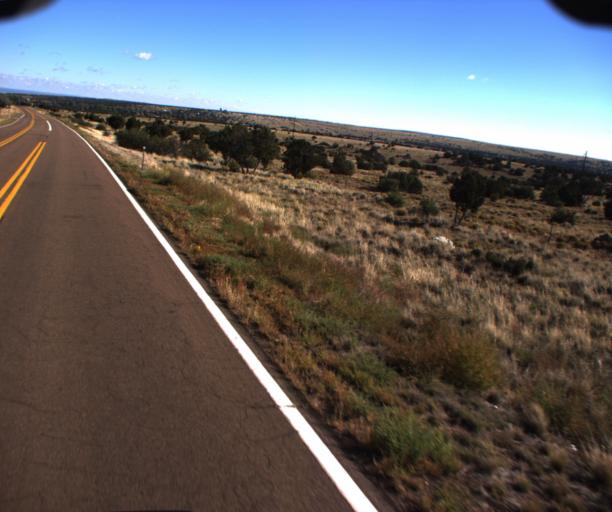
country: US
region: Arizona
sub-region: Apache County
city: Saint Johns
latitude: 34.4119
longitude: -109.6466
